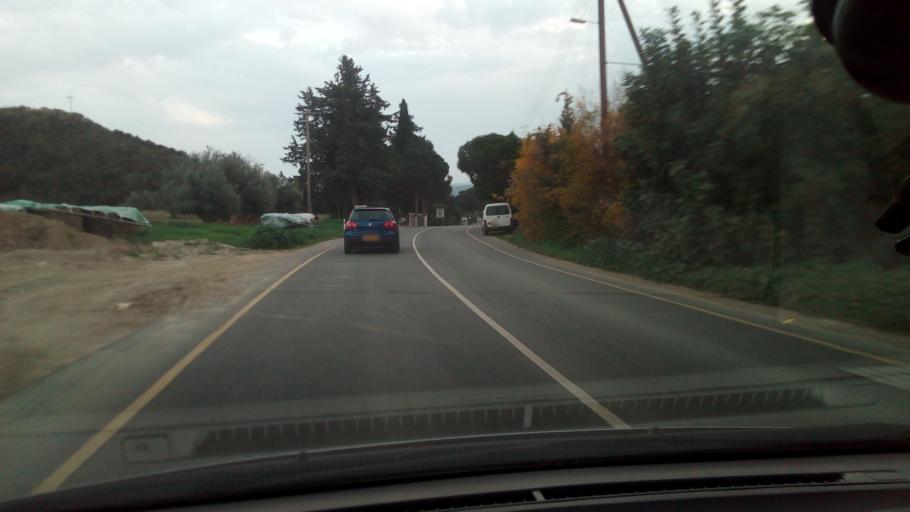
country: CY
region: Pafos
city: Polis
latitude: 35.0244
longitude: 32.4333
